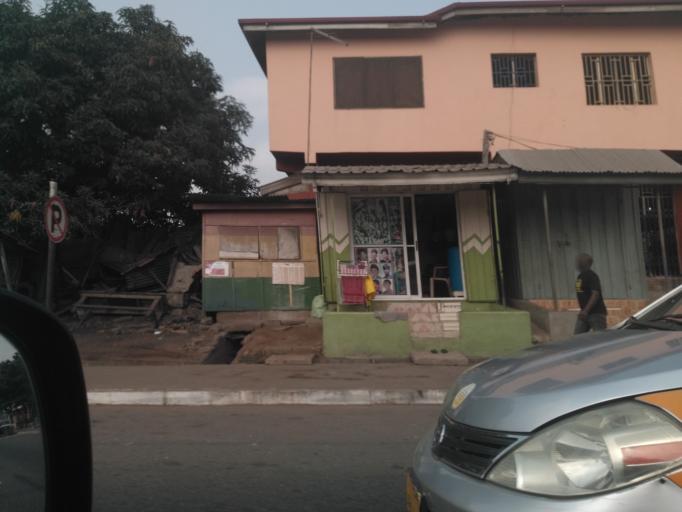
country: GH
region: Greater Accra
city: Accra
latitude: 5.5789
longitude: -0.1959
